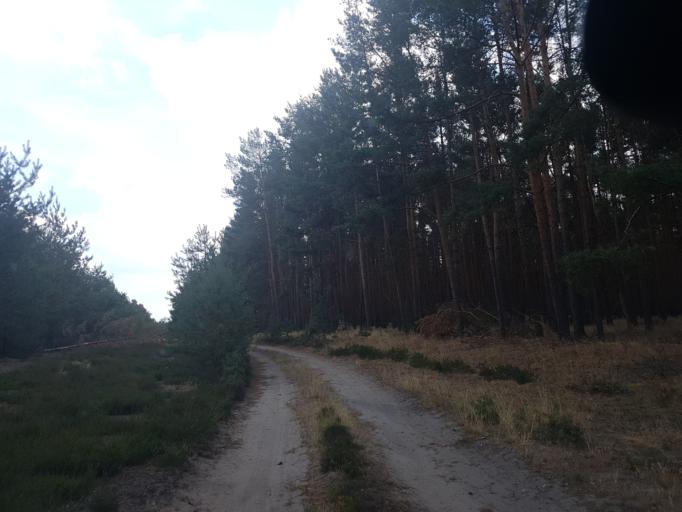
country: DE
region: Brandenburg
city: Treuenbrietzen
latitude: 52.0554
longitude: 12.8382
